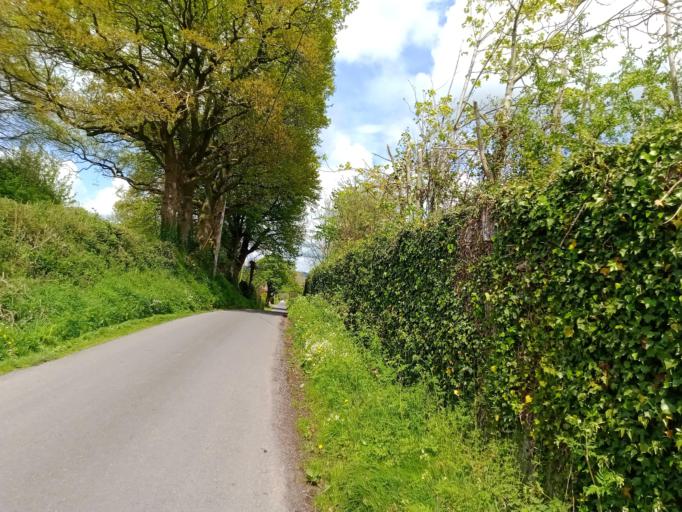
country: IE
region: Leinster
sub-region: Kilkenny
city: Ballyragget
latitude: 52.7294
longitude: -7.4177
